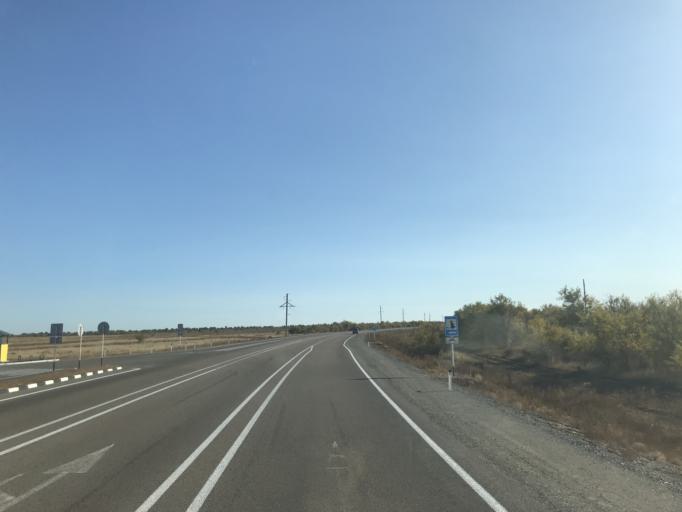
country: KZ
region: Pavlodar
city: Koktobe
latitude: 51.7280
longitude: 77.5595
